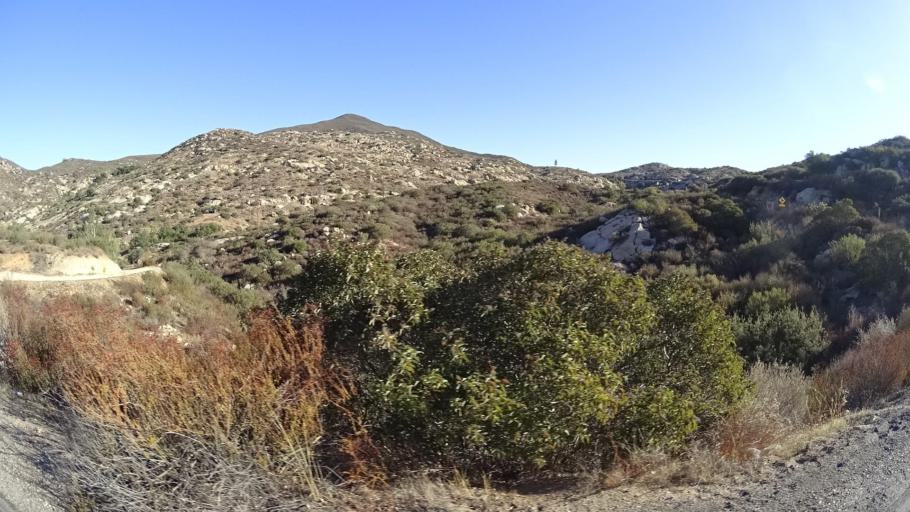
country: MX
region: Baja California
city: Tecate
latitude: 32.6006
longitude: -116.6404
